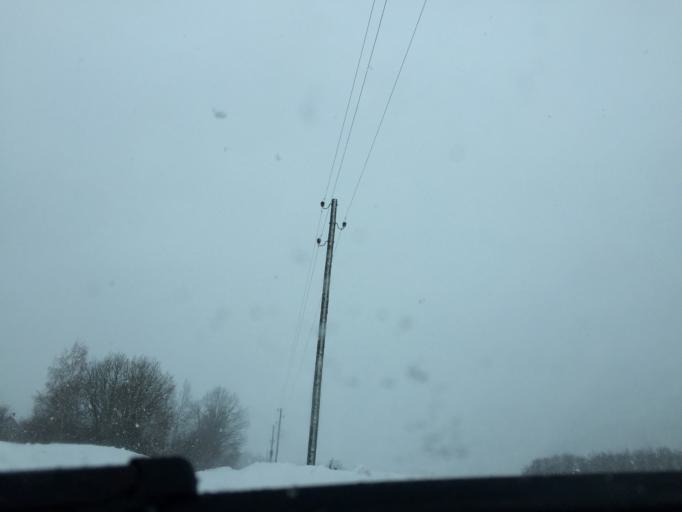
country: LV
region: Amatas Novads
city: Drabesi
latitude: 57.0639
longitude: 25.3214
